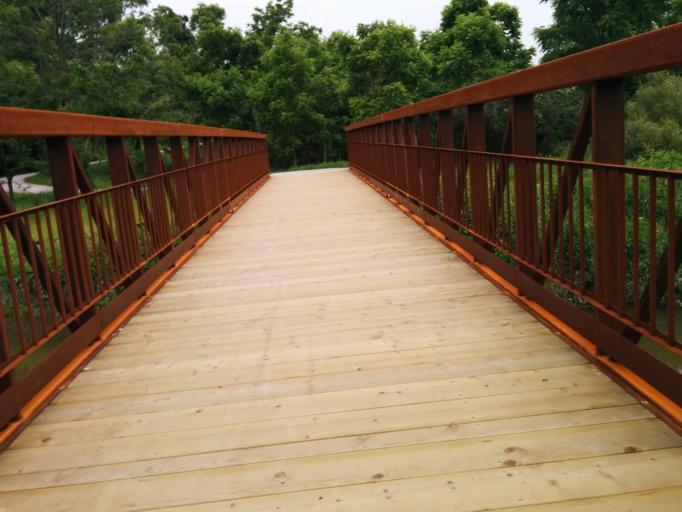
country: CA
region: Ontario
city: Brampton
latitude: 43.7489
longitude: -79.8236
